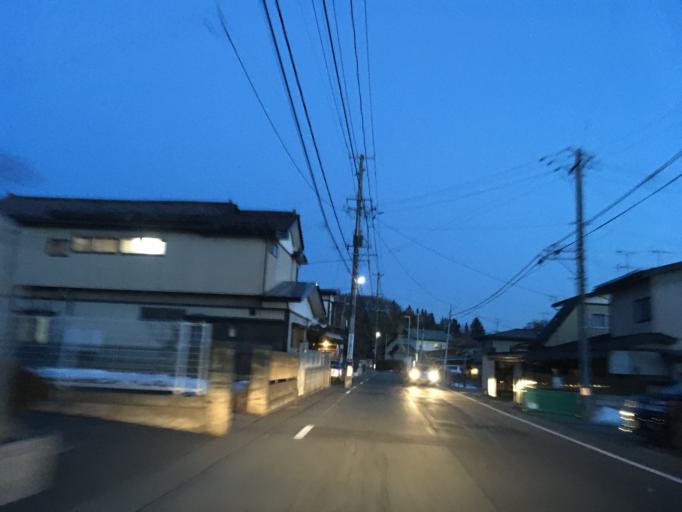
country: JP
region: Iwate
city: Morioka-shi
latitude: 39.7014
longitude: 141.1677
